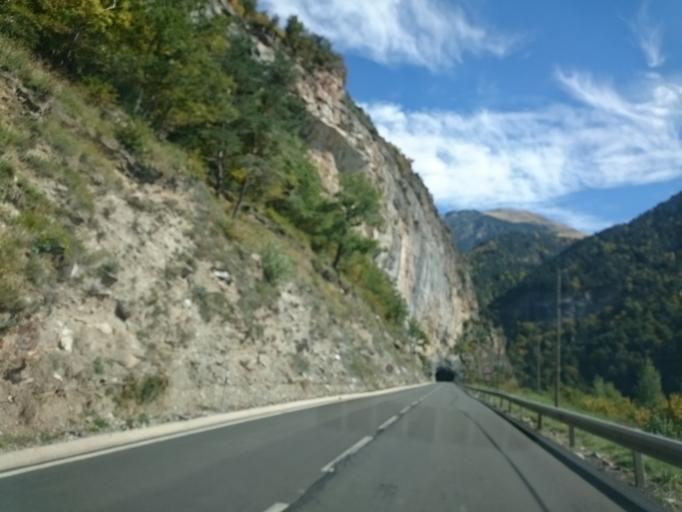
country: ES
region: Aragon
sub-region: Provincia de Huesca
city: Bonansa
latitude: 42.5465
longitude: 0.7361
